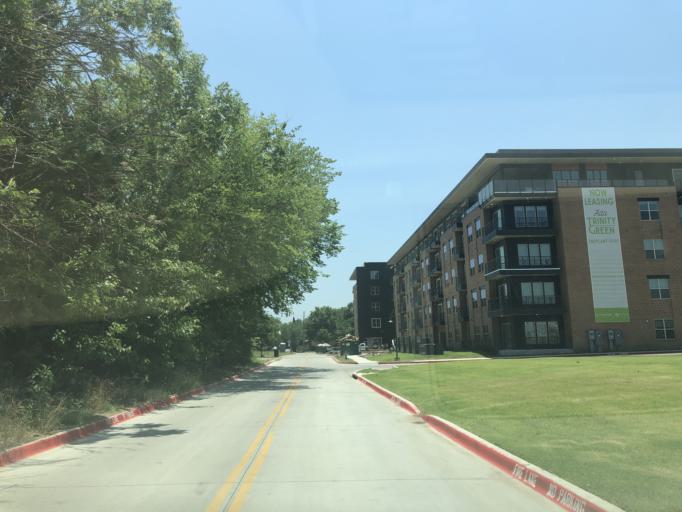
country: US
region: Texas
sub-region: Dallas County
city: Dallas
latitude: 32.7779
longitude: -96.8371
